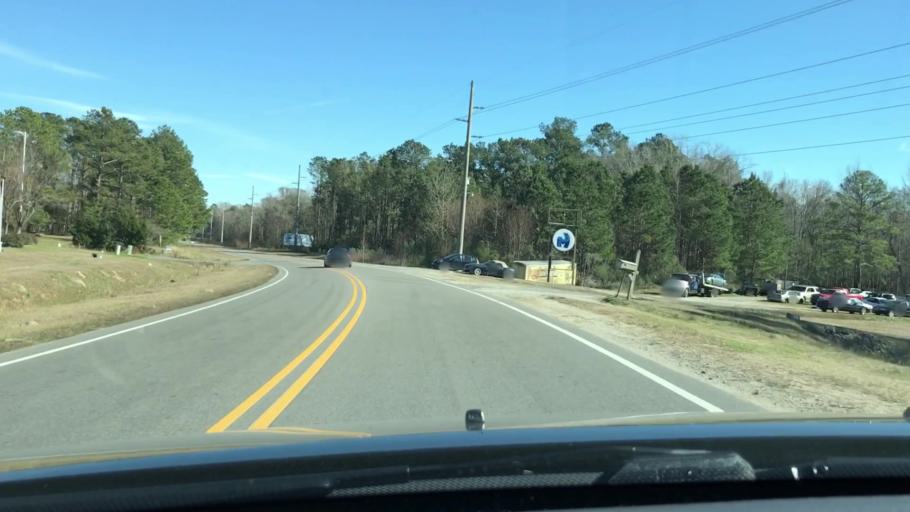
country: US
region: North Carolina
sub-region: Brunswick County
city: Shallotte
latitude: 33.9598
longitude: -78.4151
